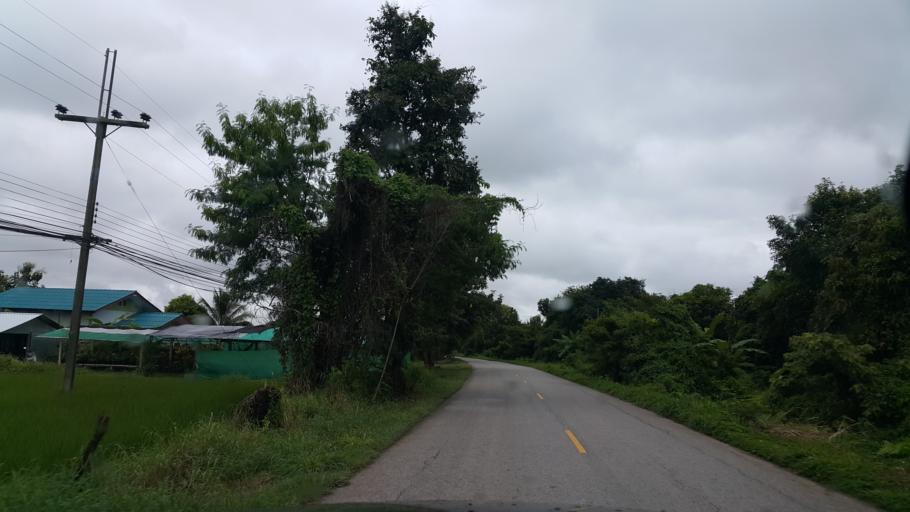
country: TH
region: Phayao
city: Chiang Kham
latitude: 19.5276
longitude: 100.3236
